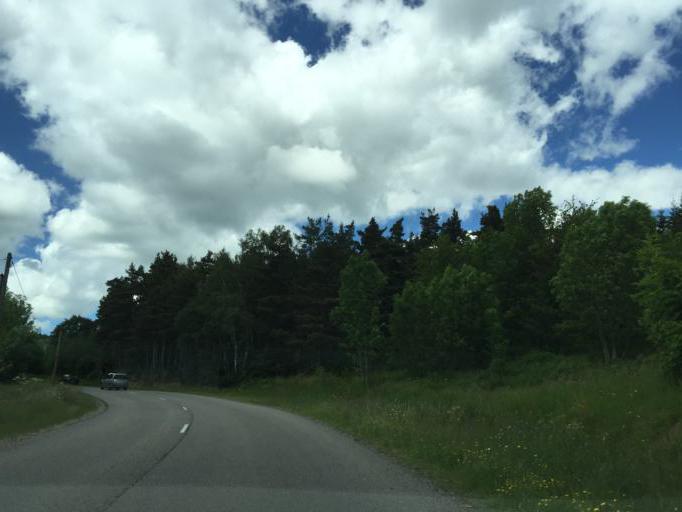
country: FR
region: Rhone-Alpes
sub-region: Departement de la Loire
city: Lezigneux
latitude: 45.5314
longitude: 3.9963
